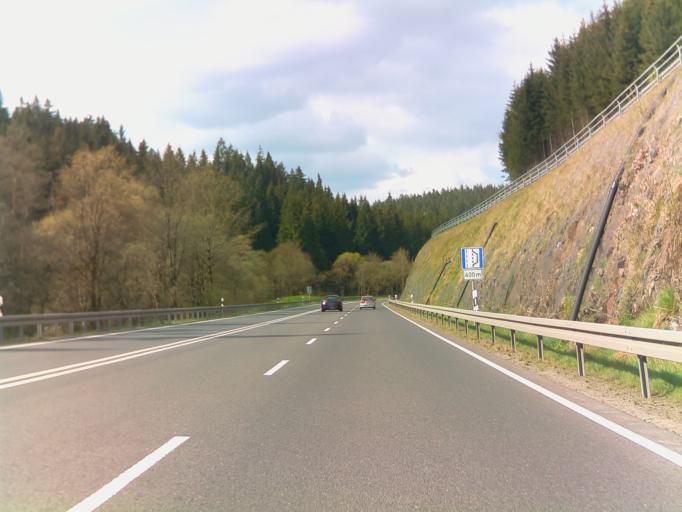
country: DE
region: Bavaria
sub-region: Upper Franconia
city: Teuschnitz
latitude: 50.4072
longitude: 11.3527
